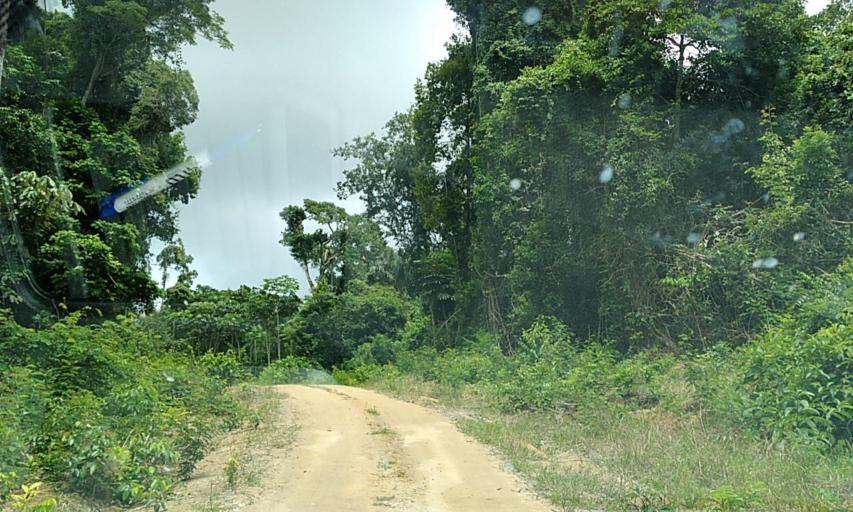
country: BR
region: Para
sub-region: Altamira
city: Altamira
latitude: -3.0573
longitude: -52.9069
